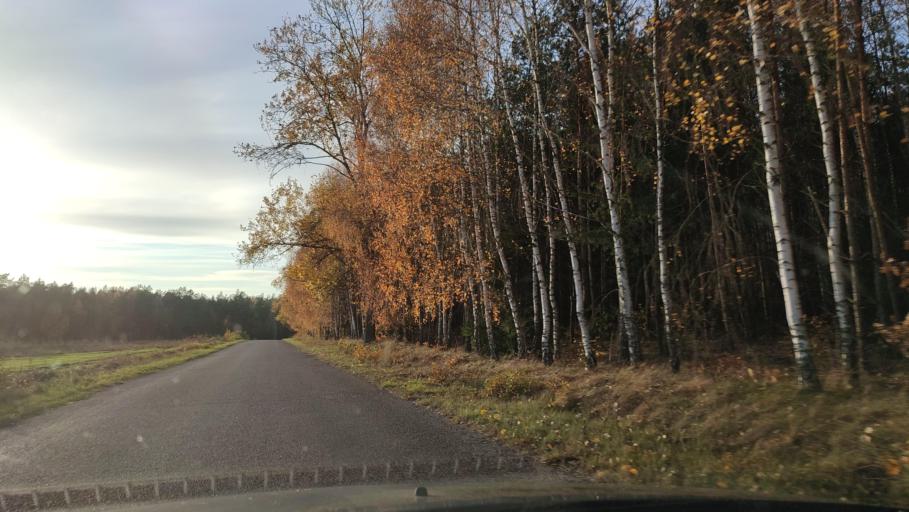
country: PL
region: Masovian Voivodeship
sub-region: Powiat przasnyski
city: Chorzele
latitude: 53.3312
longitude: 20.7375
